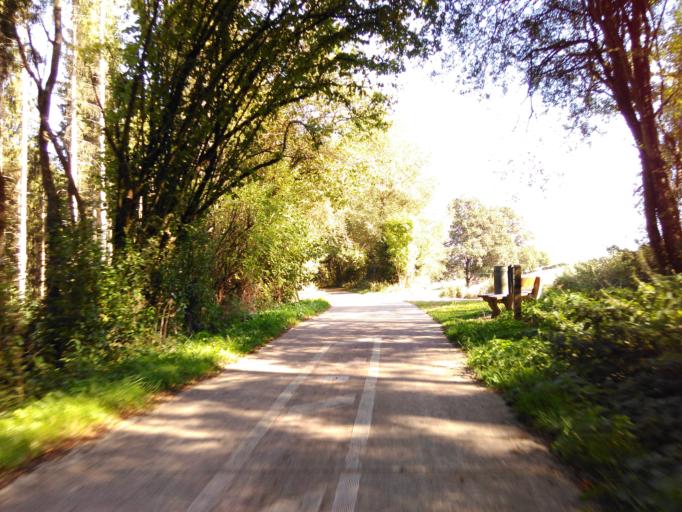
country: LU
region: Diekirch
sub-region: Canton de Redange
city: Beckerich
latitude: 49.7164
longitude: 5.9053
